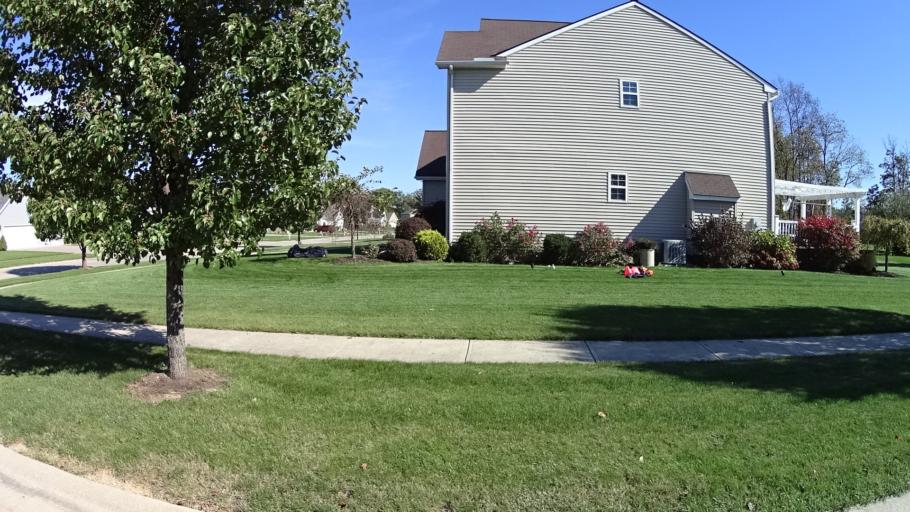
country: US
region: Ohio
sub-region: Lorain County
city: Amherst
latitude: 41.3868
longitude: -82.2403
